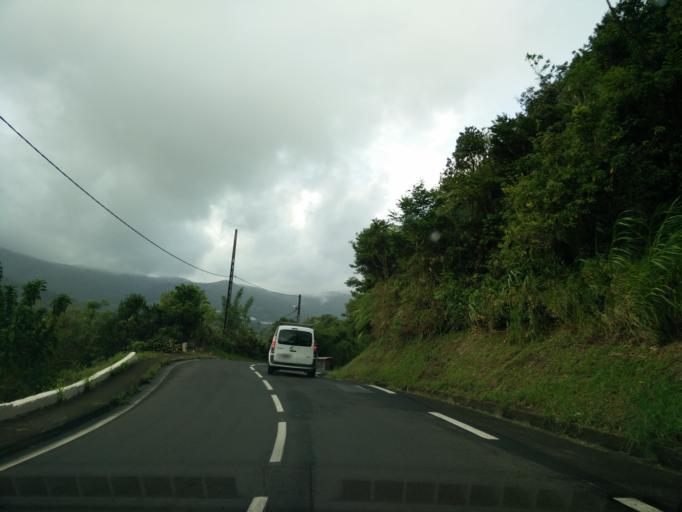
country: MQ
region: Martinique
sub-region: Martinique
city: Le Morne-Rouge
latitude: 14.7717
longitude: -61.1306
